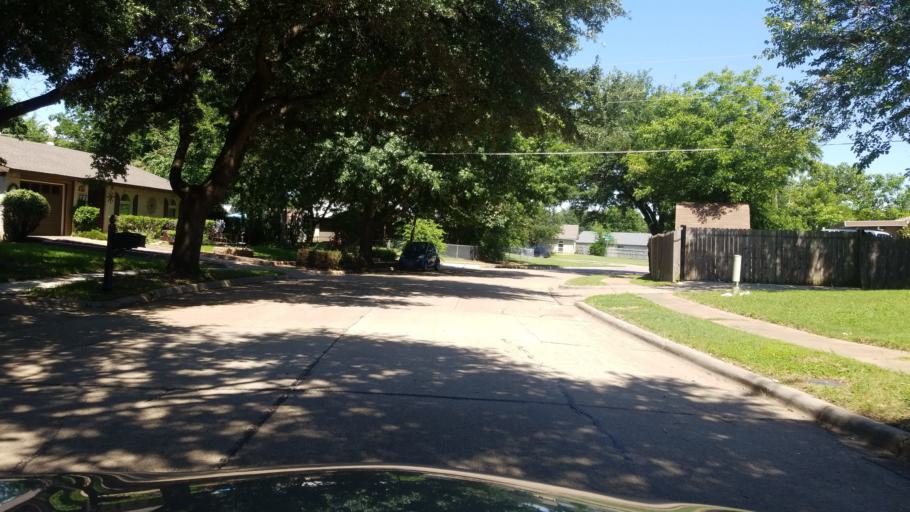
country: US
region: Texas
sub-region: Dallas County
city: Grand Prairie
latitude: 32.6923
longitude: -96.9971
